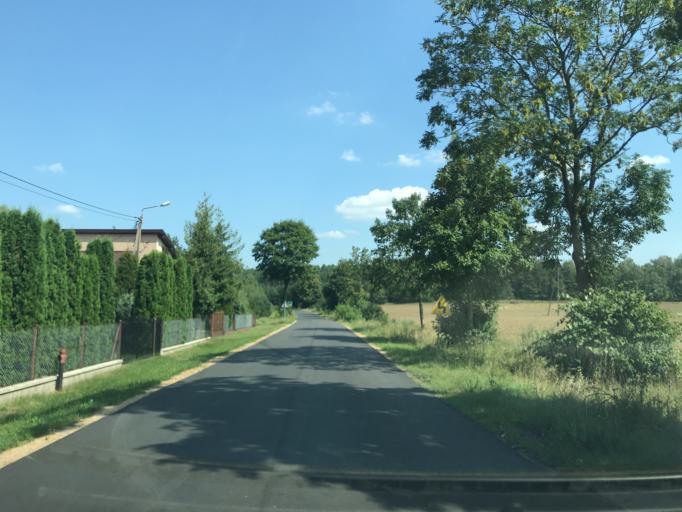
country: PL
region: Masovian Voivodeship
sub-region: Powiat zurominski
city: Lubowidz
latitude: 53.1748
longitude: 19.8598
